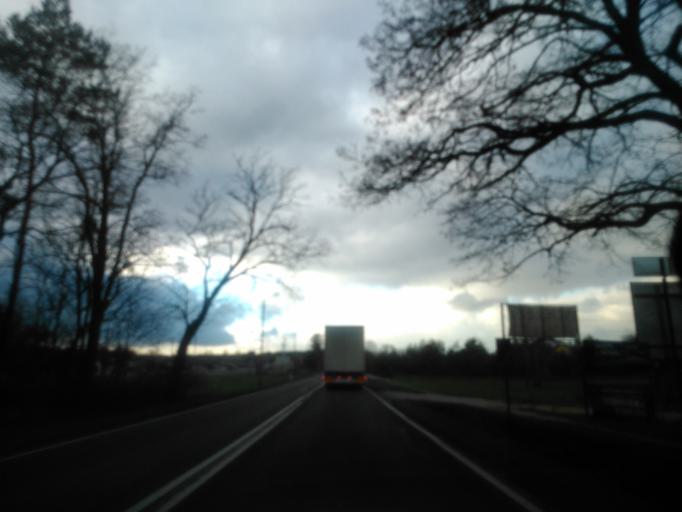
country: PL
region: Masovian Voivodeship
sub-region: Powiat nowodworski
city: Nowy Dwor Mazowiecki
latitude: 52.3942
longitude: 20.6698
